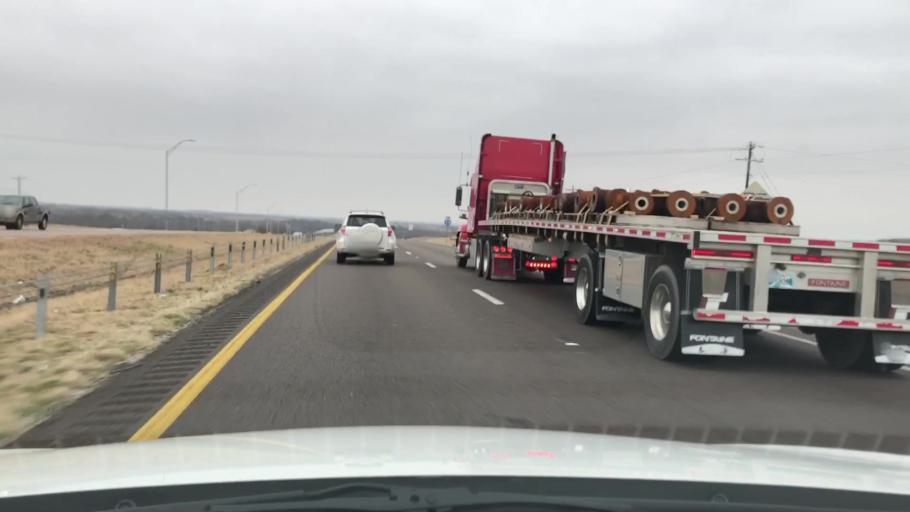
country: US
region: Texas
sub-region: Cooke County
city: Gainesville
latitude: 33.6881
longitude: -97.1598
